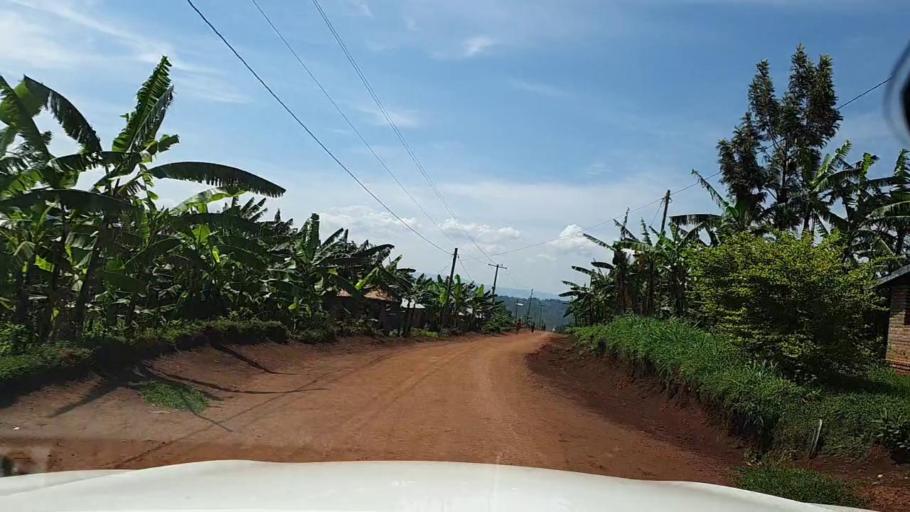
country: RW
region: Southern Province
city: Butare
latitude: -2.7098
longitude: 29.8394
